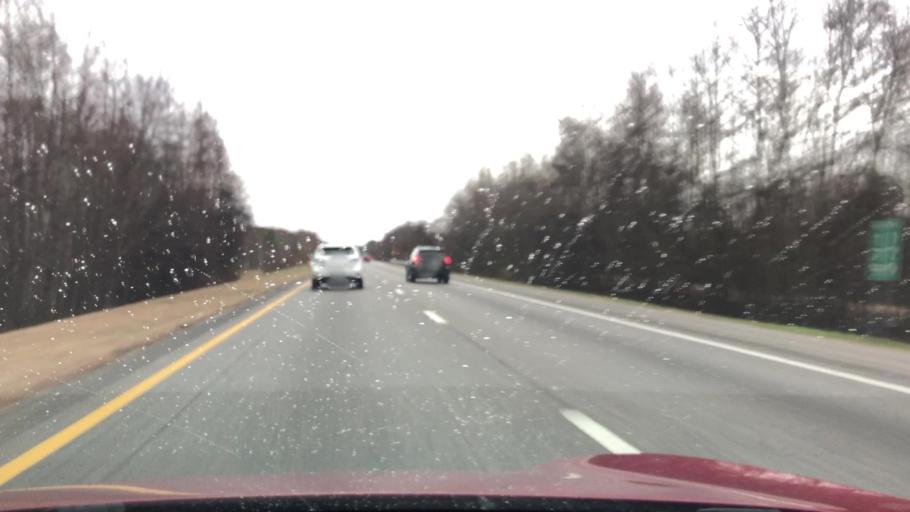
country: US
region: South Carolina
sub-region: Dillon County
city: Latta
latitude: 34.3267
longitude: -79.5728
